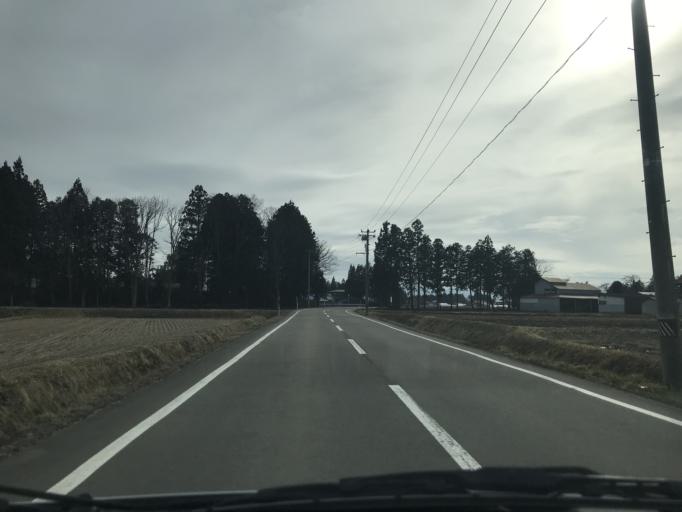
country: JP
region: Iwate
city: Hanamaki
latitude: 39.3559
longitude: 141.0634
